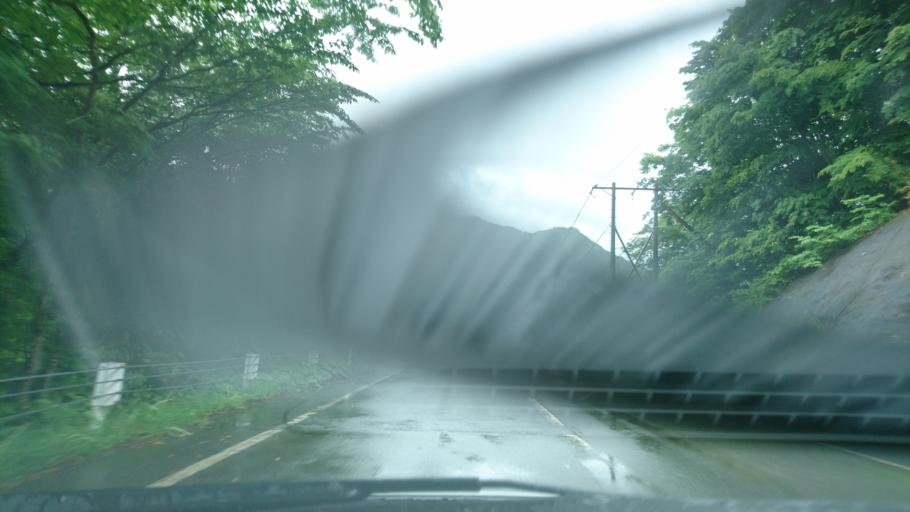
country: JP
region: Iwate
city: Ichinoseki
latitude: 39.0047
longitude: 140.8608
